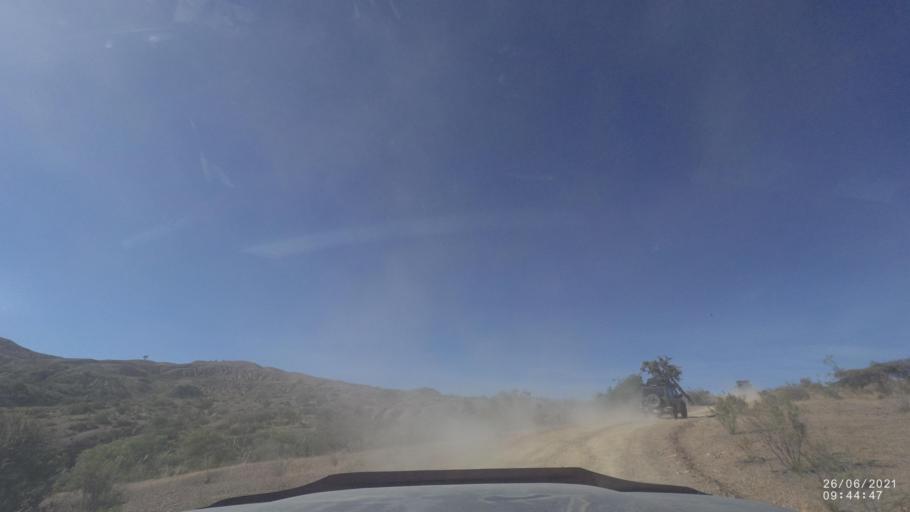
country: BO
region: Cochabamba
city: Mizque
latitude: -17.9460
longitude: -65.6319
